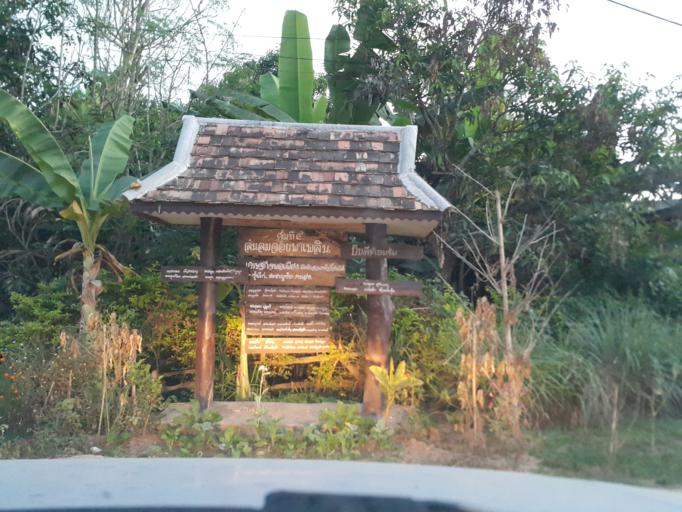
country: TH
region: Lamphun
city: Mae Tha
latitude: 18.5456
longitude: 99.2460
